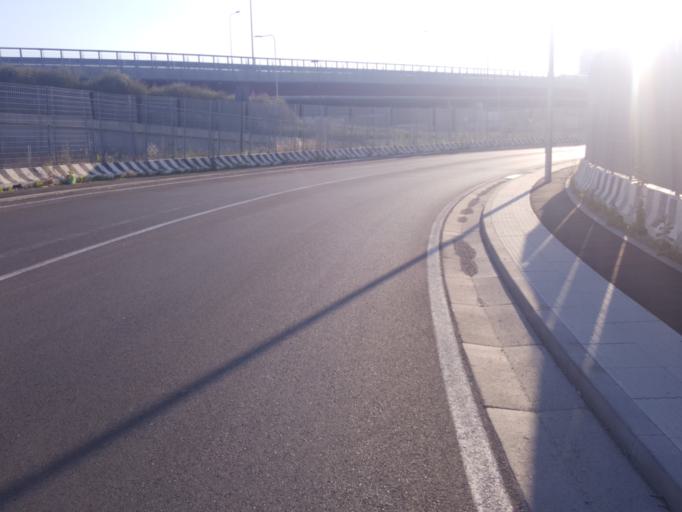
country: IT
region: Liguria
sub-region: Provincia di Genova
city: San Teodoro
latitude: 44.4122
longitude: 8.8719
